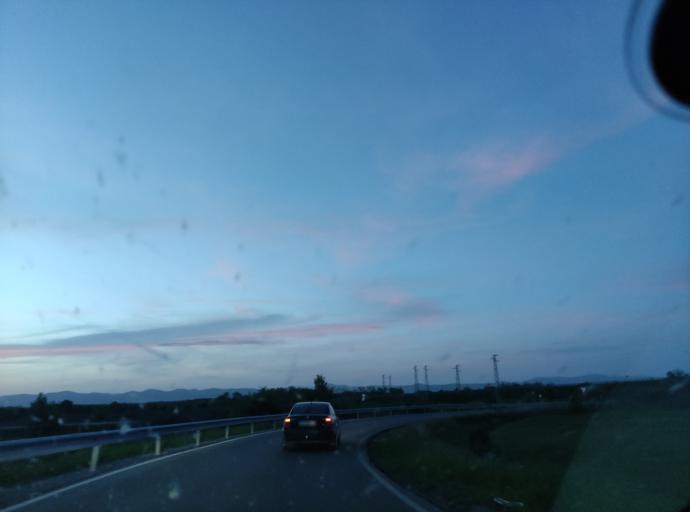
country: BG
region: Stara Zagora
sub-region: Obshtina Stara Zagora
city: Stara Zagora
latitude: 42.3379
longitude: 25.6605
